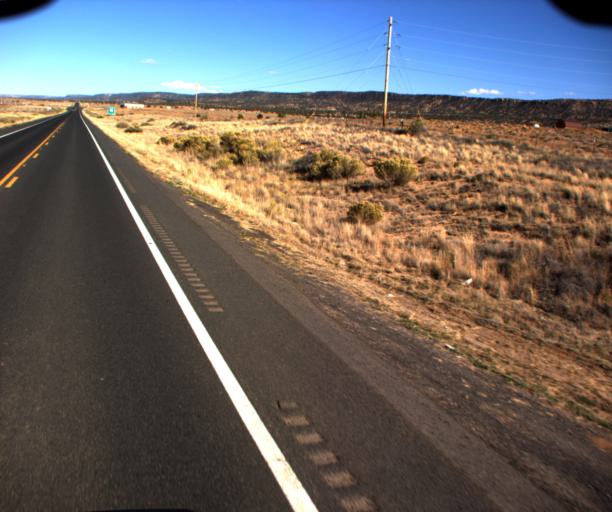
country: US
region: Arizona
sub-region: Coconino County
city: Kaibito
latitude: 36.4573
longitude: -110.7013
